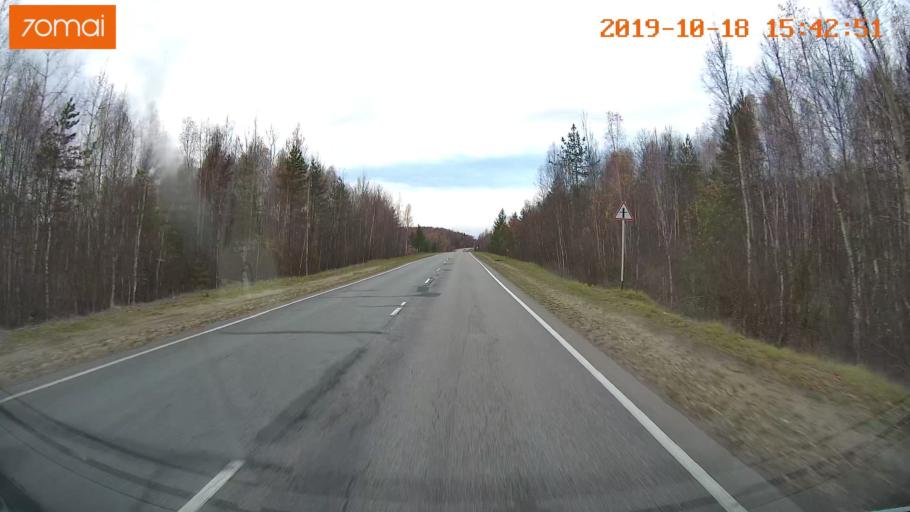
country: RU
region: Vladimir
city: Golovino
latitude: 55.9600
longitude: 40.5614
